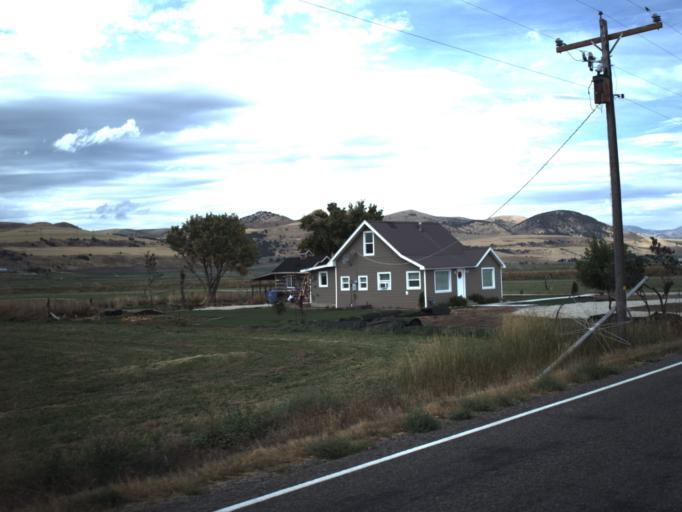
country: US
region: Utah
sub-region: Cache County
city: Lewiston
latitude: 41.9430
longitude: -111.9537
